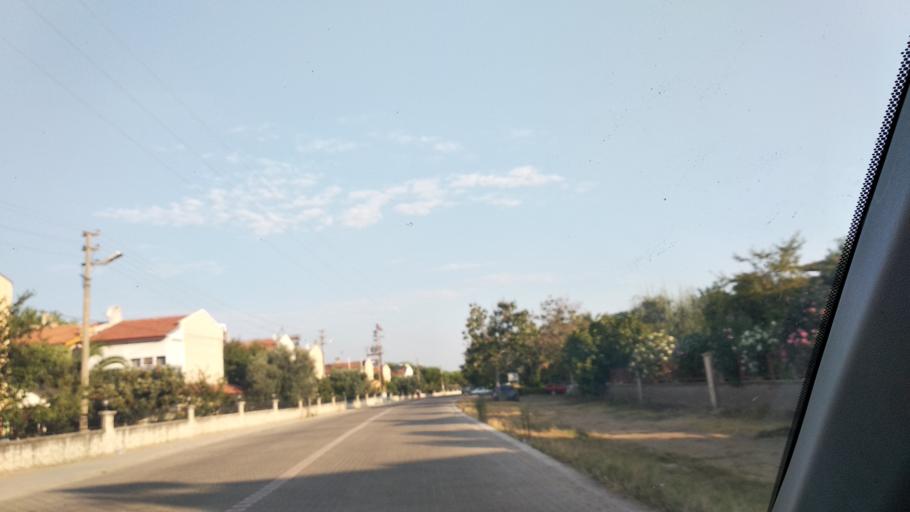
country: TR
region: Balikesir
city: Altinova
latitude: 39.1554
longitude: 26.8255
